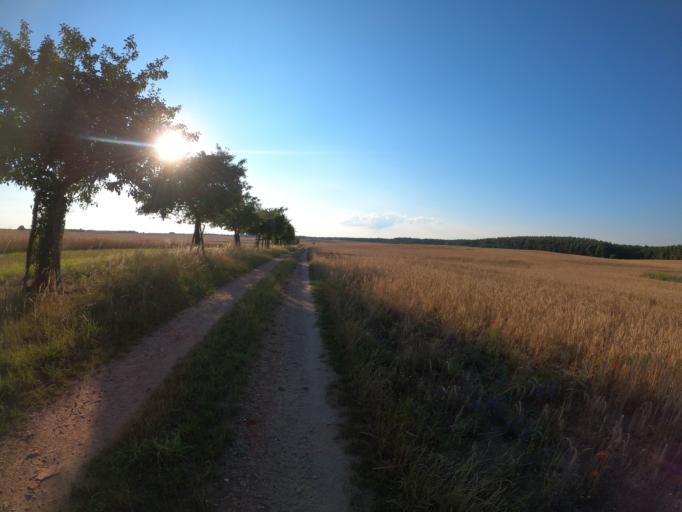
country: DE
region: Brandenburg
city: Althuttendorf
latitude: 53.0293
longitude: 13.8842
